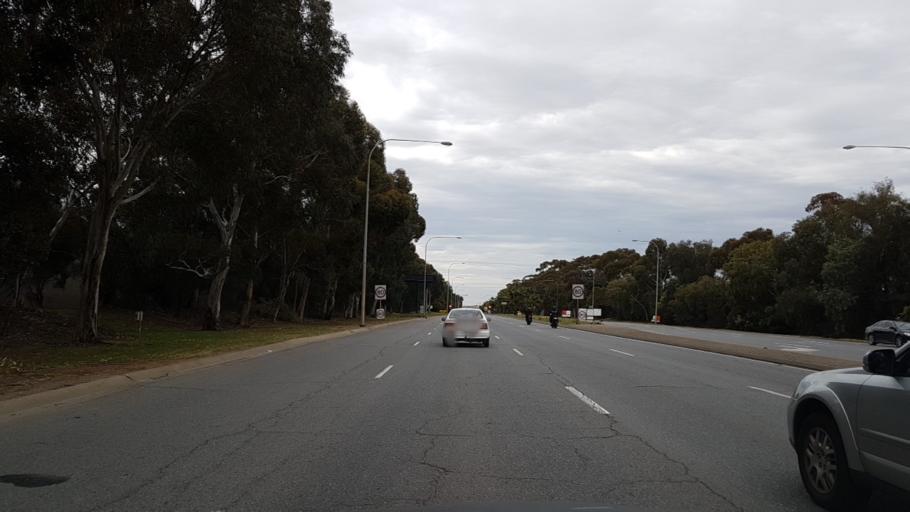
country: AU
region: South Australia
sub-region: Port Adelaide Enfield
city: Enfield
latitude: -34.8266
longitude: 138.5983
